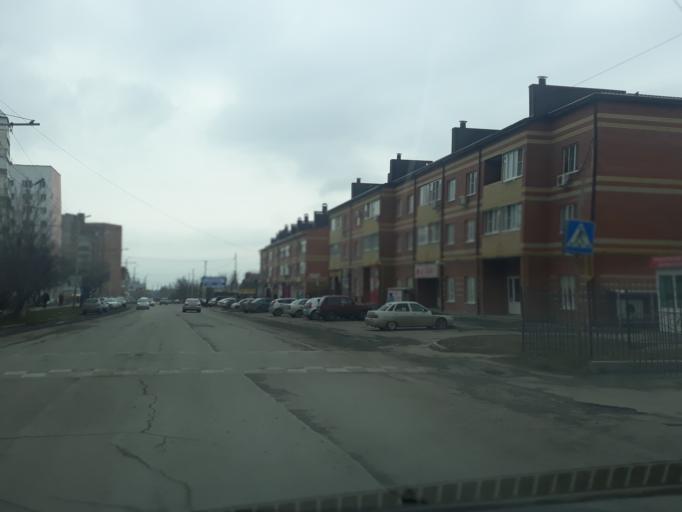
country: RU
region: Rostov
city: Taganrog
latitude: 47.2783
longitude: 38.9248
